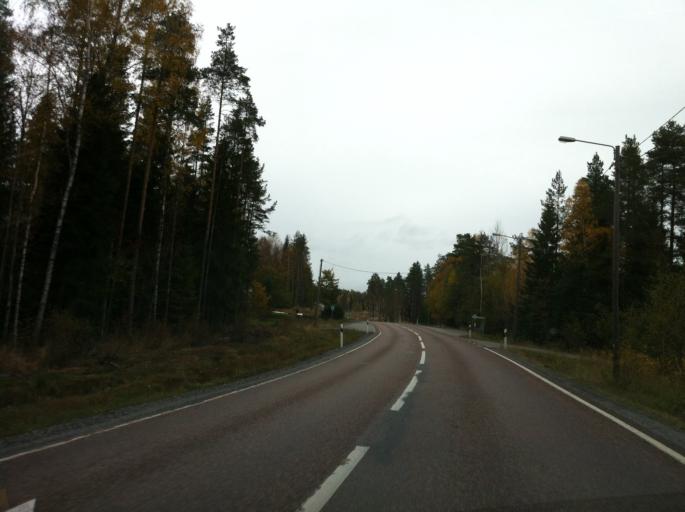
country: SE
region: Dalarna
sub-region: Ludvika Kommun
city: Grangesberg
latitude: 60.0378
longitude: 14.9681
